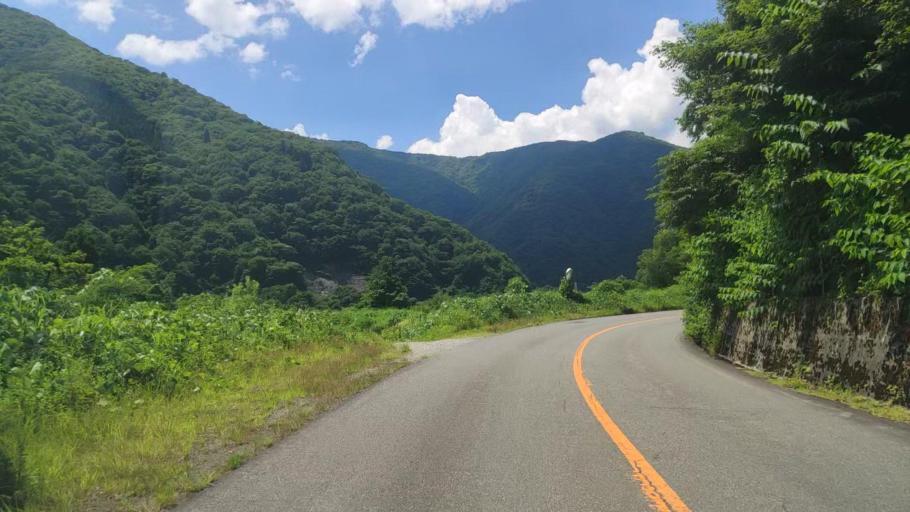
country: JP
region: Fukui
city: Ono
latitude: 35.9040
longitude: 136.5321
